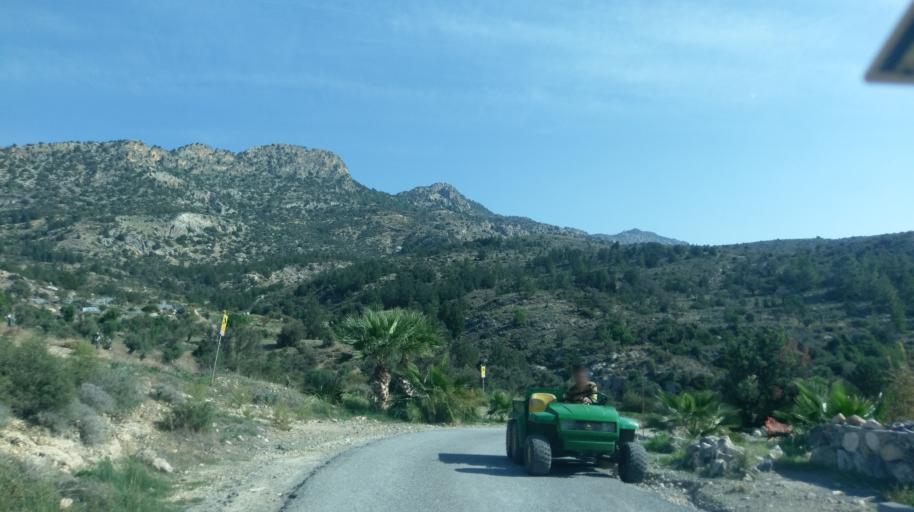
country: CY
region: Keryneia
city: Kyrenia
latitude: 35.2773
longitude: 33.3861
